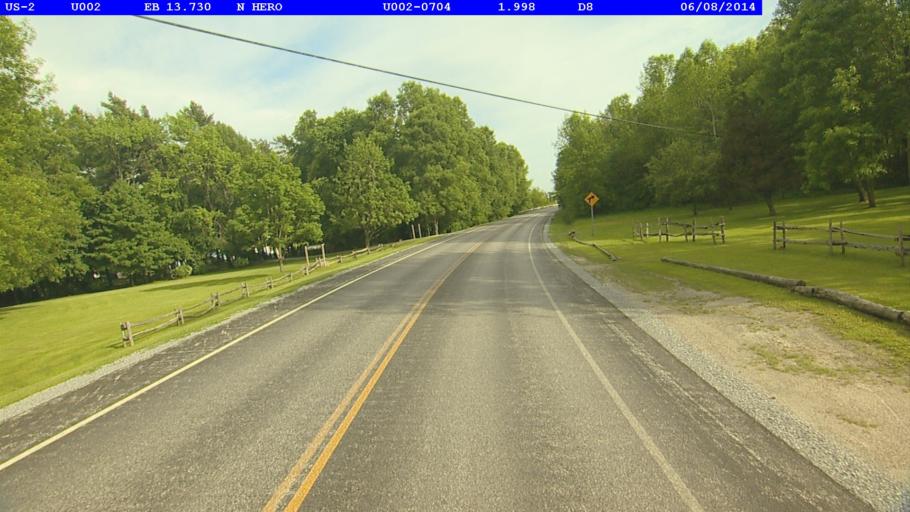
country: US
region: Vermont
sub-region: Grand Isle County
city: North Hero
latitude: 44.8612
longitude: -73.2593
